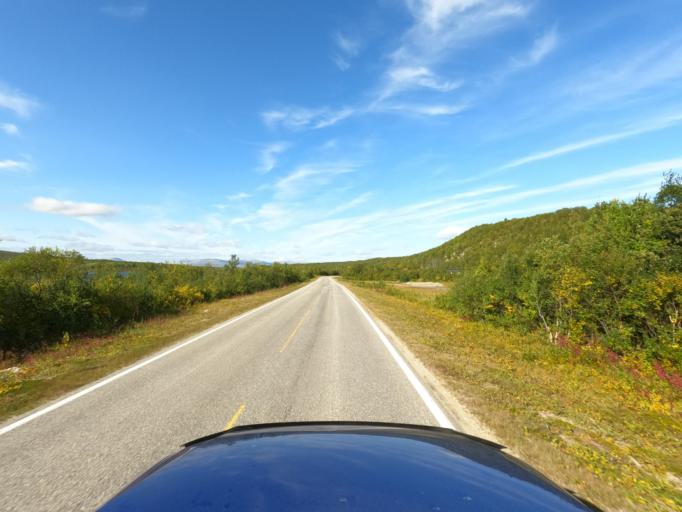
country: NO
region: Finnmark Fylke
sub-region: Porsanger
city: Lakselv
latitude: 69.7580
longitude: 25.2099
